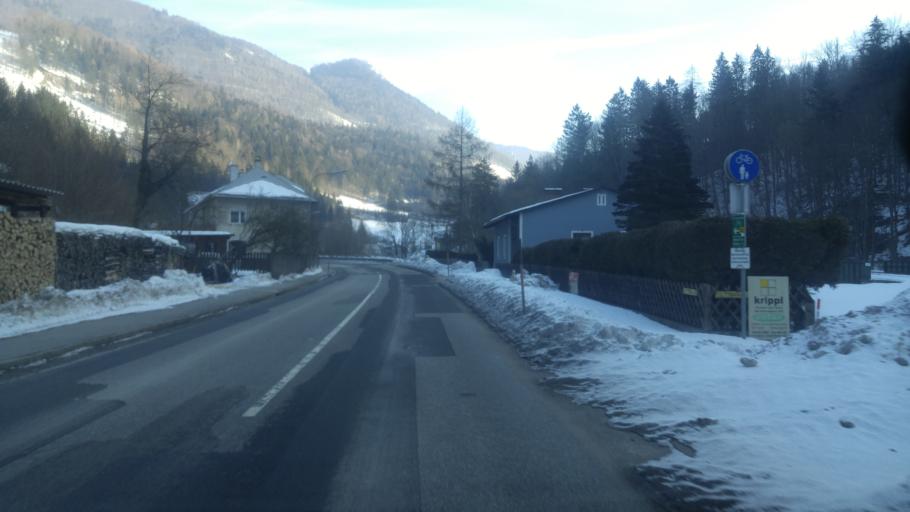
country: AT
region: Lower Austria
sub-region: Politischer Bezirk Lilienfeld
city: Lilienfeld
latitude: 47.9704
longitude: 15.5751
